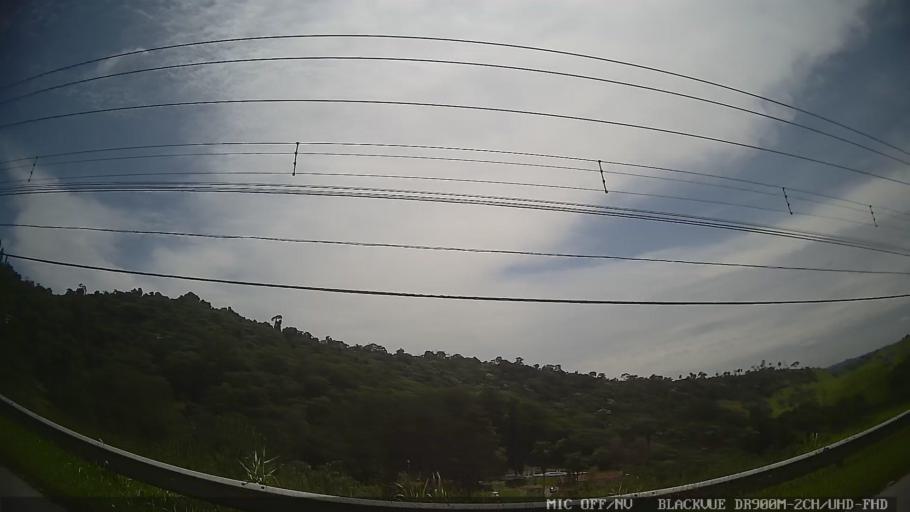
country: BR
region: Sao Paulo
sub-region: Santa Isabel
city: Santa Isabel
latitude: -23.3497
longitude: -46.2002
